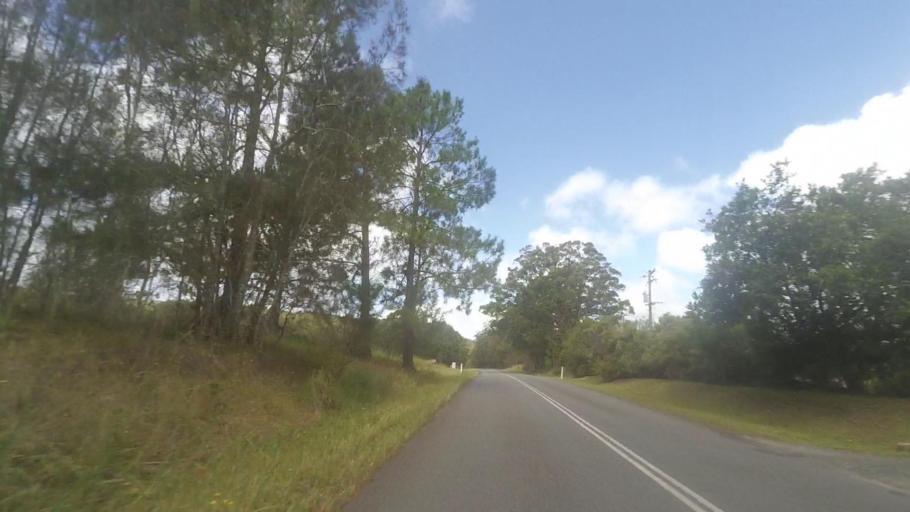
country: AU
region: New South Wales
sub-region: Great Lakes
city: Bulahdelah
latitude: -32.3884
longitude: 152.4198
